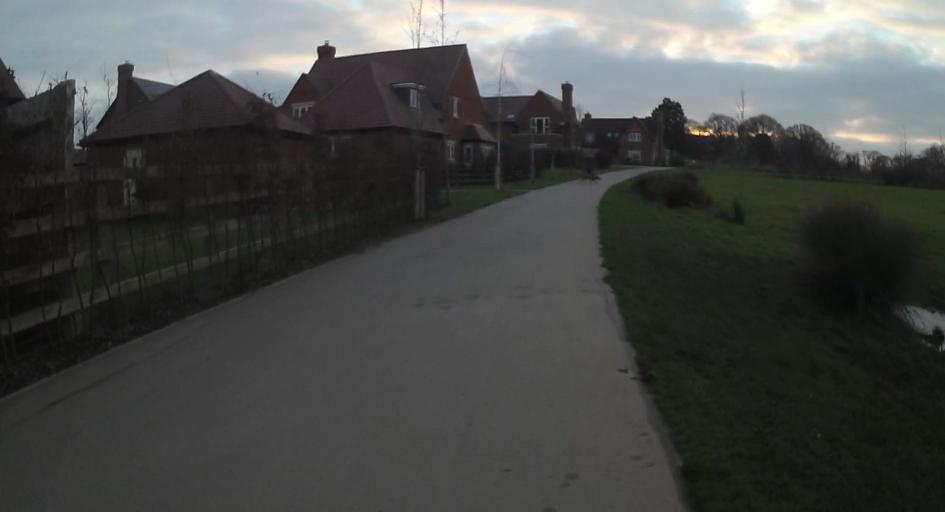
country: GB
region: England
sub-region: Bracknell Forest
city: Bracknell
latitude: 51.4311
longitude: -0.7608
